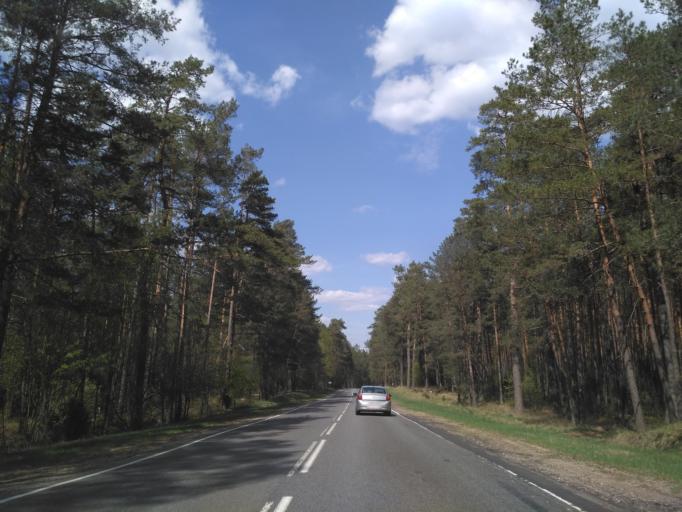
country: BY
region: Minsk
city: Myadzyel
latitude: 54.7993
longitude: 26.9414
